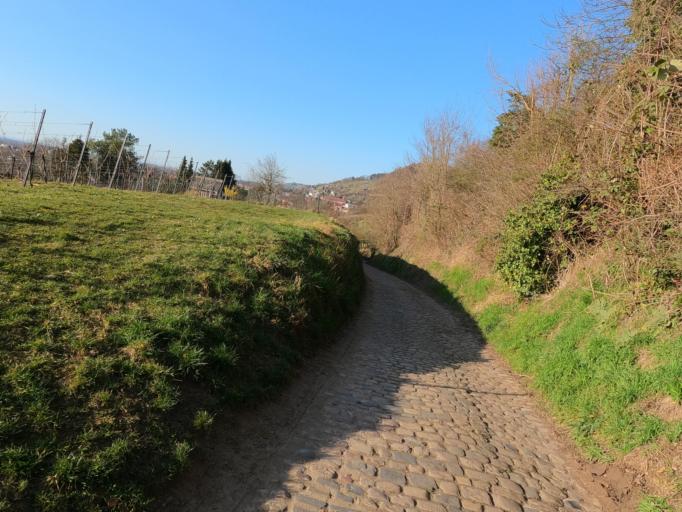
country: DE
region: Hesse
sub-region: Regierungsbezirk Darmstadt
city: Heppenheim an der Bergstrasse
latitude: 49.6320
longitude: 8.6458
